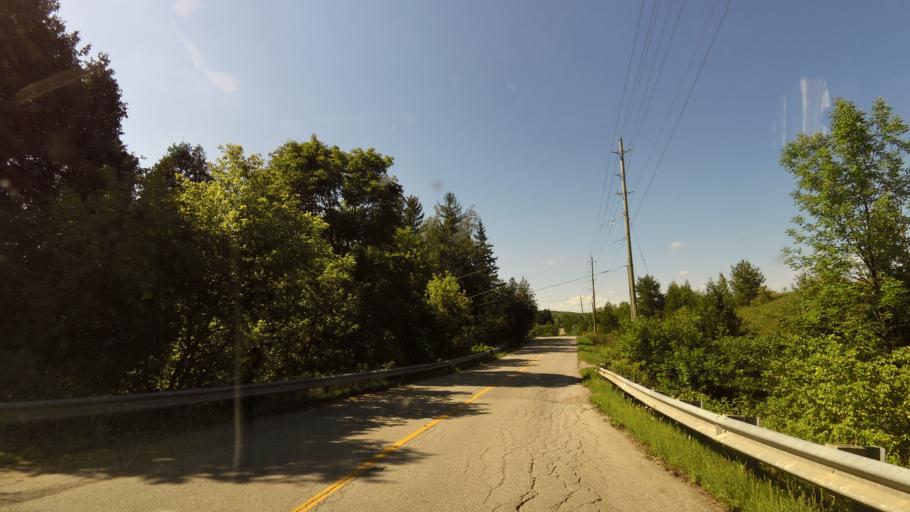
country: CA
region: Ontario
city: Brampton
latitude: 43.7712
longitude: -79.9236
